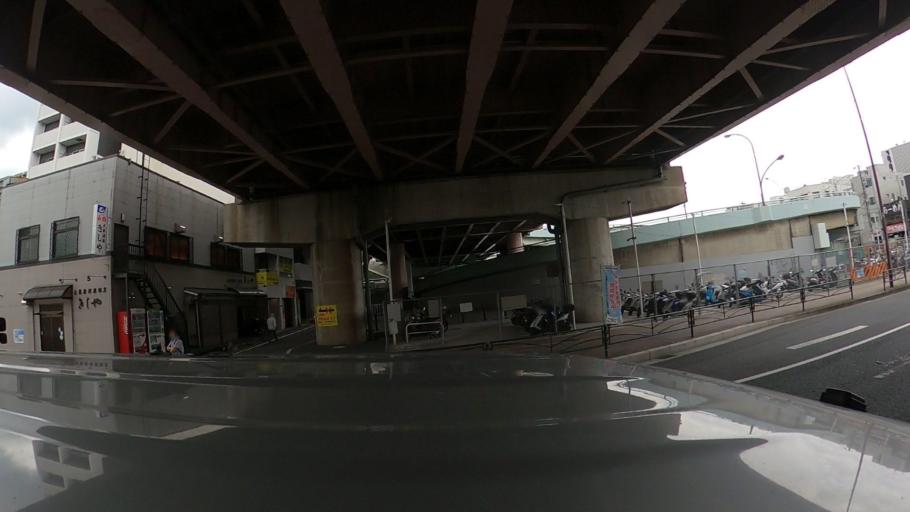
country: JP
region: Kanagawa
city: Yokohama
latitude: 35.4862
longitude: 139.6549
